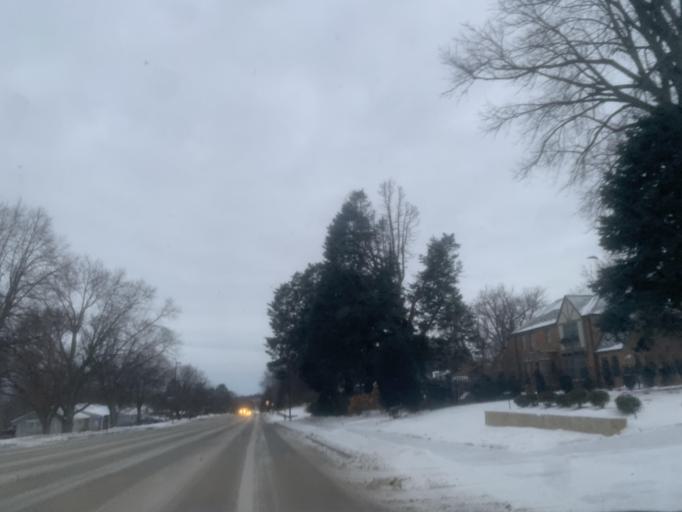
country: US
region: Nebraska
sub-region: Douglas County
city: Ralston
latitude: 41.2462
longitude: -96.0527
